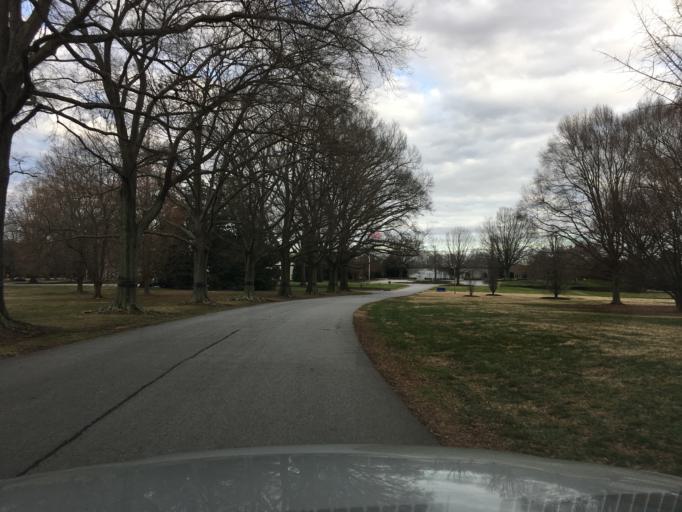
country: US
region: South Carolina
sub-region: Spartanburg County
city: Saxon
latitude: 34.9895
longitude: -81.9602
